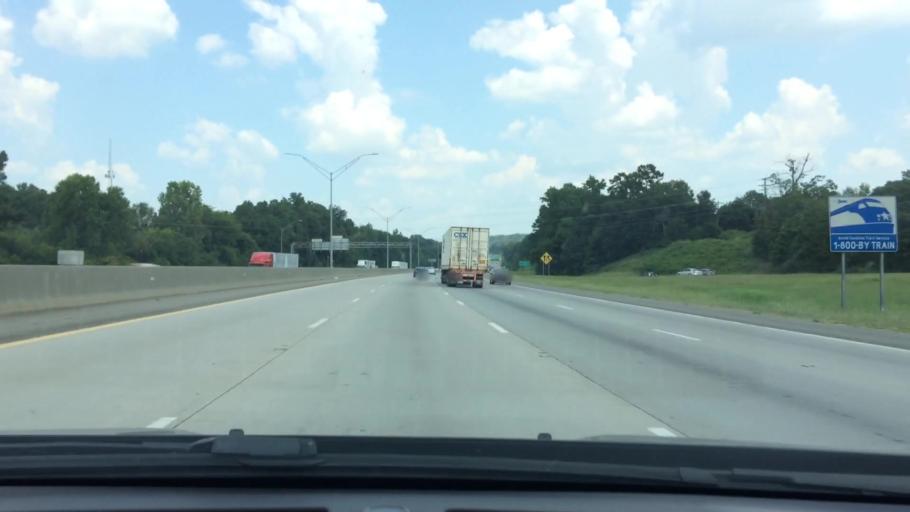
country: US
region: North Carolina
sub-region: Cabarrus County
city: Harrisburg
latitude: 35.3134
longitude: -80.7577
